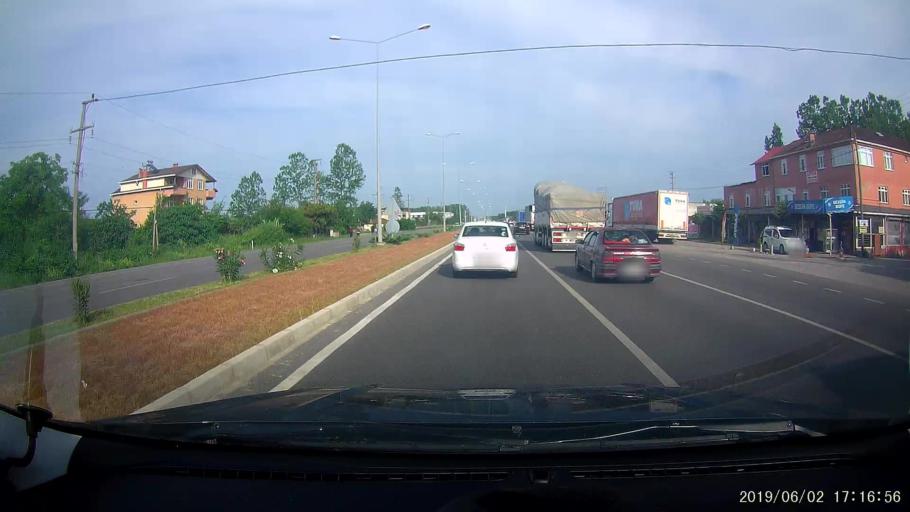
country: TR
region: Samsun
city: Dikbiyik
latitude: 41.2320
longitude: 36.5739
